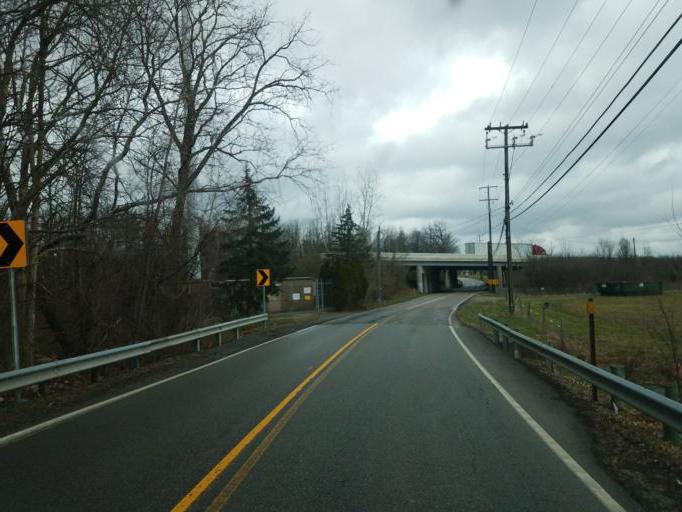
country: US
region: Ohio
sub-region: Franklin County
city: Westerville
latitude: 40.1678
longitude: -82.9608
